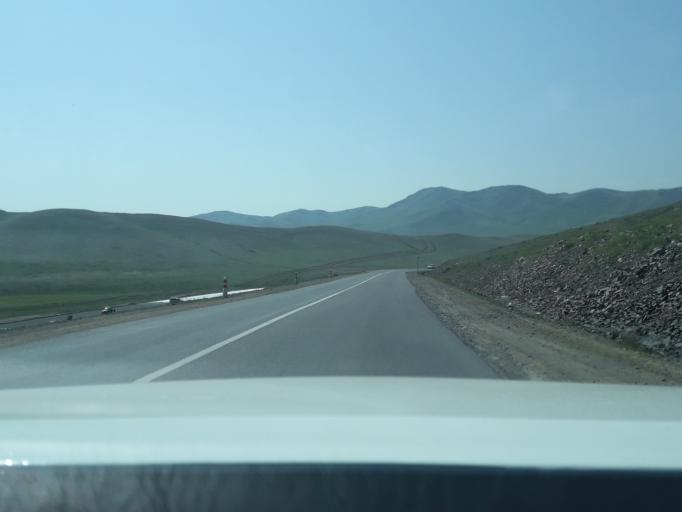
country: MN
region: Ulaanbaatar
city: Ulaanbaatar
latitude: 47.7855
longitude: 106.7486
